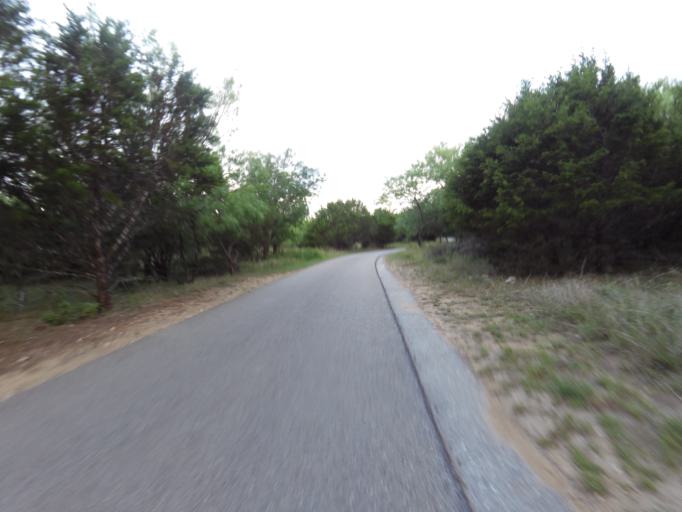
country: US
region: Texas
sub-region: Bexar County
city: Helotes
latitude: 29.5635
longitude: -98.6239
